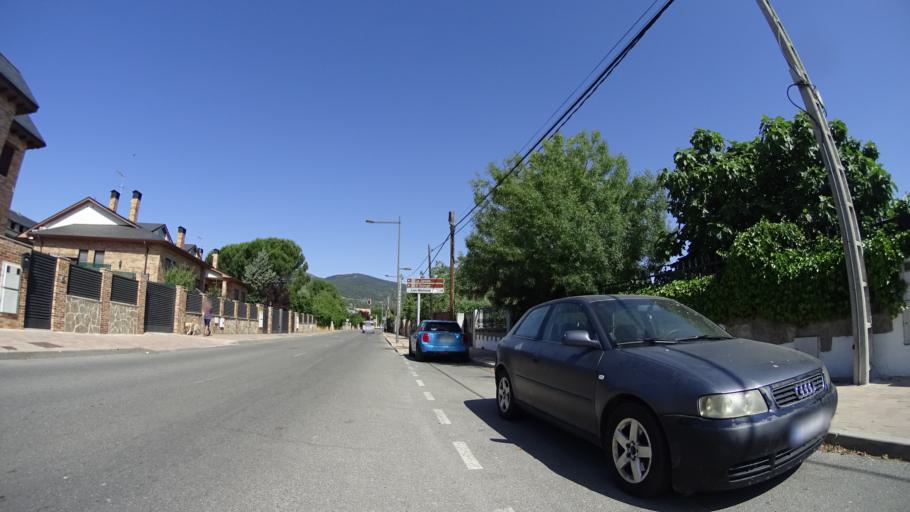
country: ES
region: Madrid
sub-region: Provincia de Madrid
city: Guadarrama
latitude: 40.6778
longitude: -4.0927
